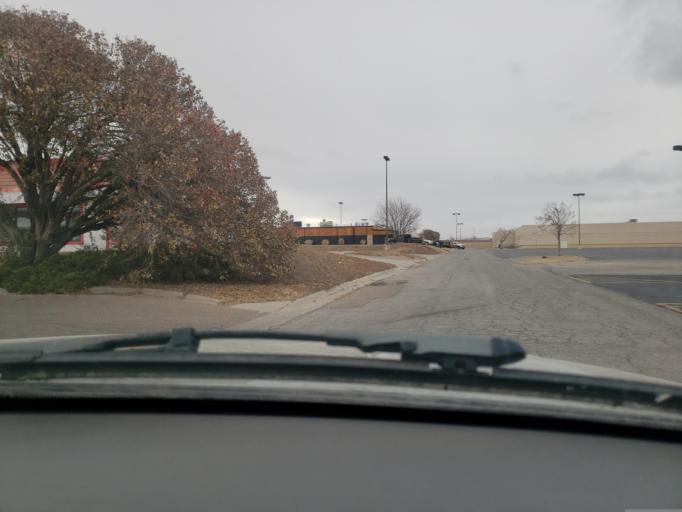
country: US
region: Kansas
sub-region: Finney County
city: Garden City
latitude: 37.9769
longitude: -100.8435
